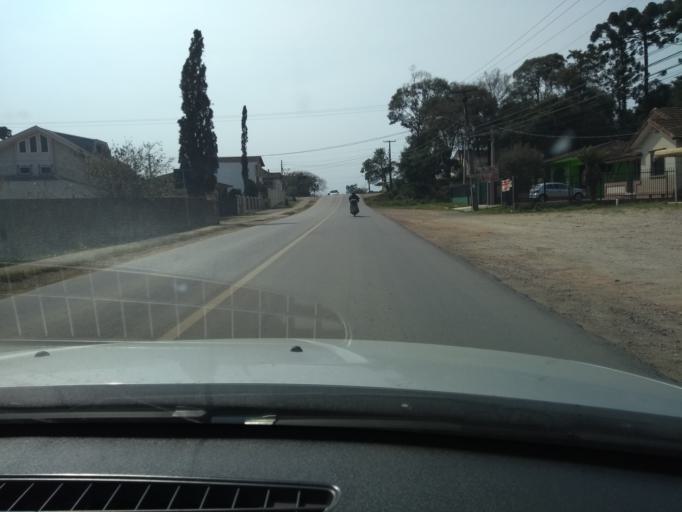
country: BR
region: Parana
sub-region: Araucaria
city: Araucaria
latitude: -25.6154
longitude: -49.3436
